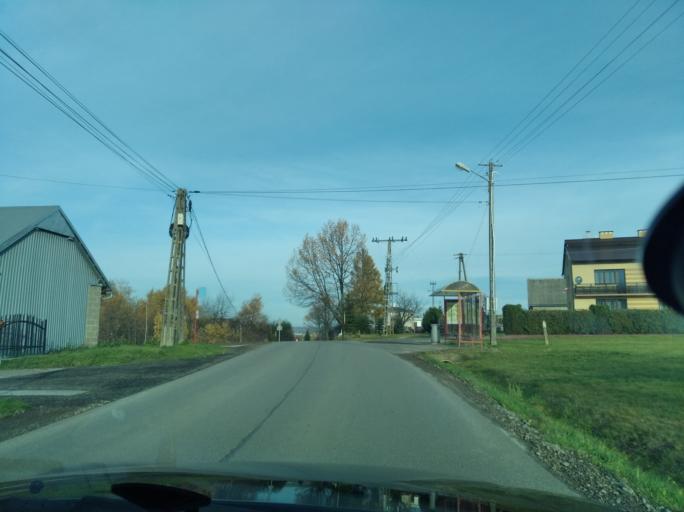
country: PL
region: Subcarpathian Voivodeship
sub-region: Powiat rzeszowski
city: Siedliska
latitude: 49.9379
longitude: 21.9799
